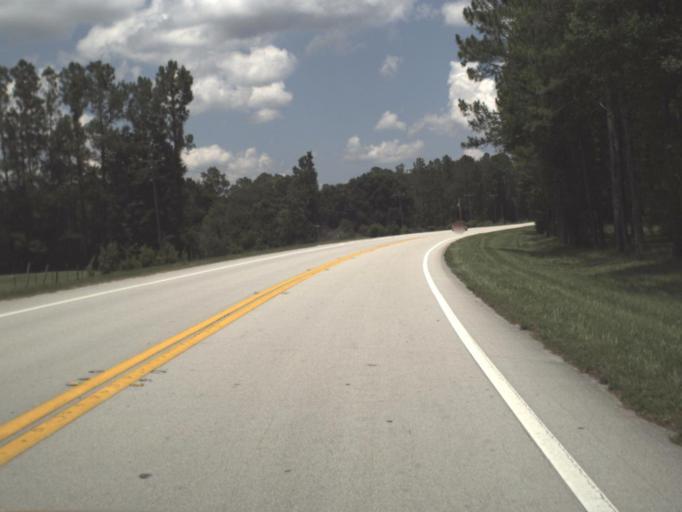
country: US
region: Florida
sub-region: Baker County
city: Macclenny
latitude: 30.1690
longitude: -82.1830
